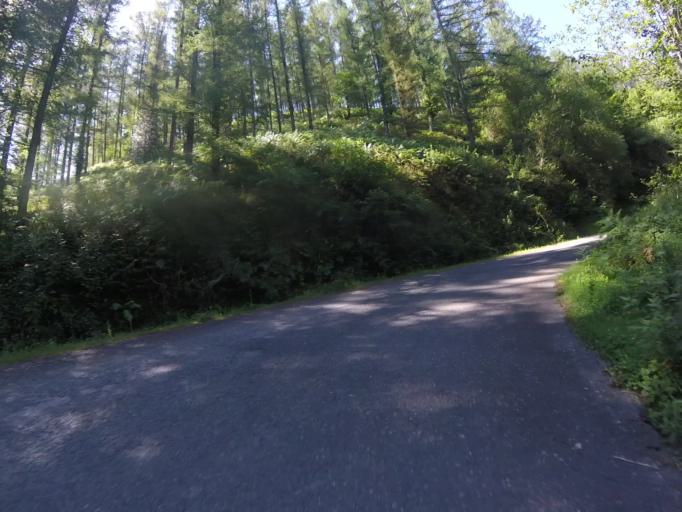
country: ES
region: Navarre
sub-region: Provincia de Navarra
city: Goizueta
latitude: 43.1850
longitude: -1.8232
